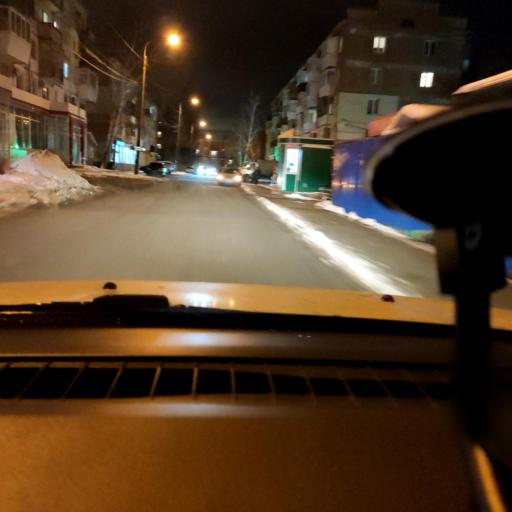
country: RU
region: Samara
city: Volzhskiy
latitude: 53.3483
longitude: 50.2196
